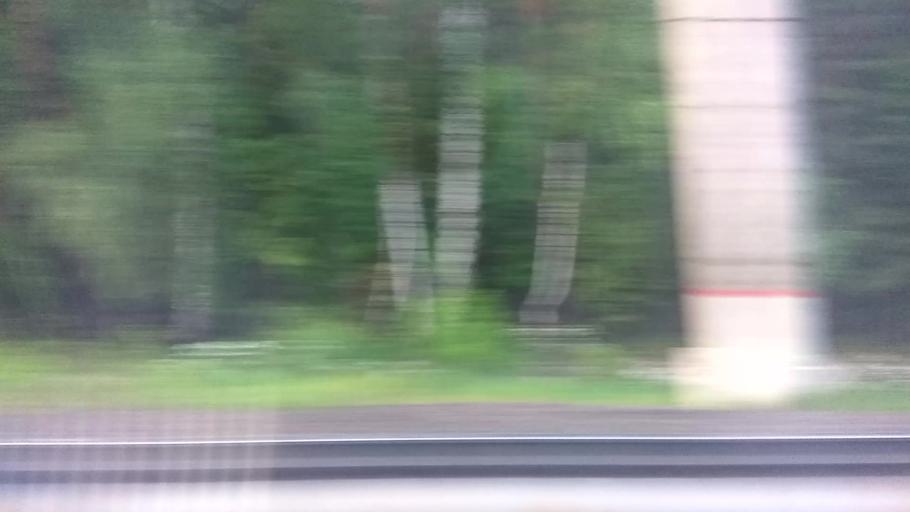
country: RU
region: Moskovskaya
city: Vostryakovo
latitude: 55.3664
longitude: 37.8266
